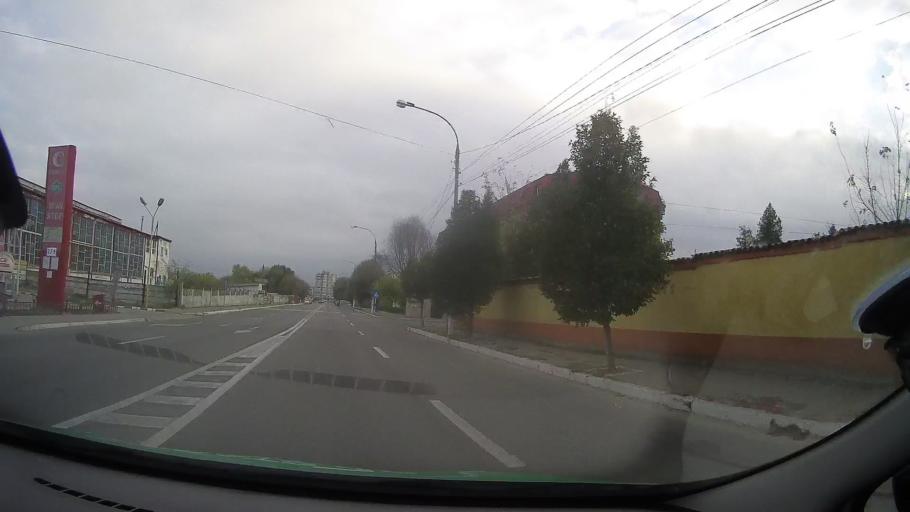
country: RO
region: Constanta
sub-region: Municipiul Medgidia
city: Medgidia
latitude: 44.2651
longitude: 28.2590
